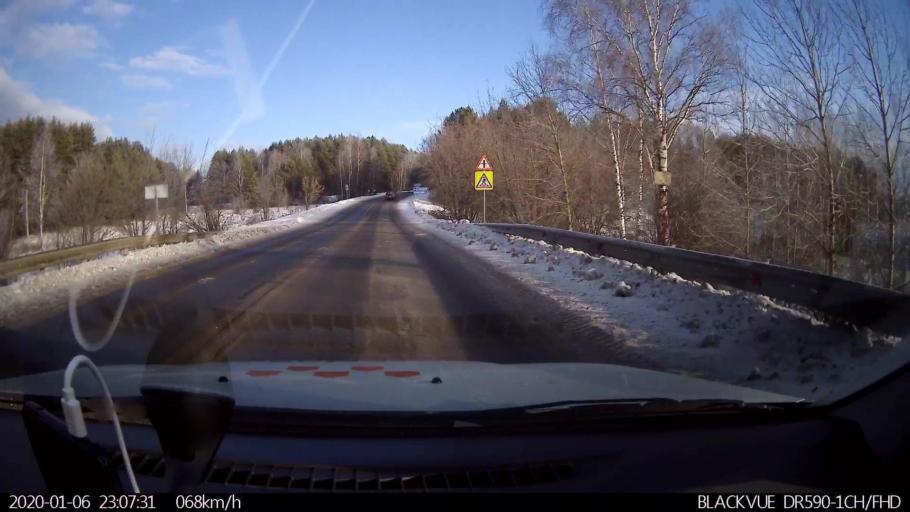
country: RU
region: Nizjnij Novgorod
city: Bogorodsk
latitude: 56.1292
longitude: 43.5917
